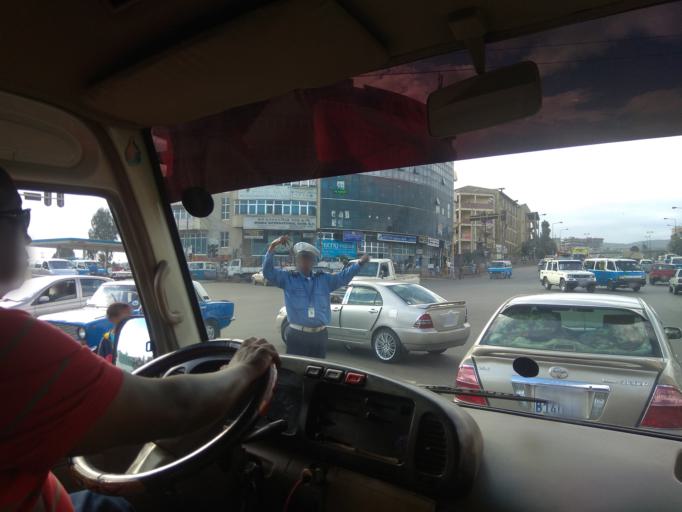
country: ET
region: Adis Abeba
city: Addis Ababa
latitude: 9.0334
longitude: 38.7146
